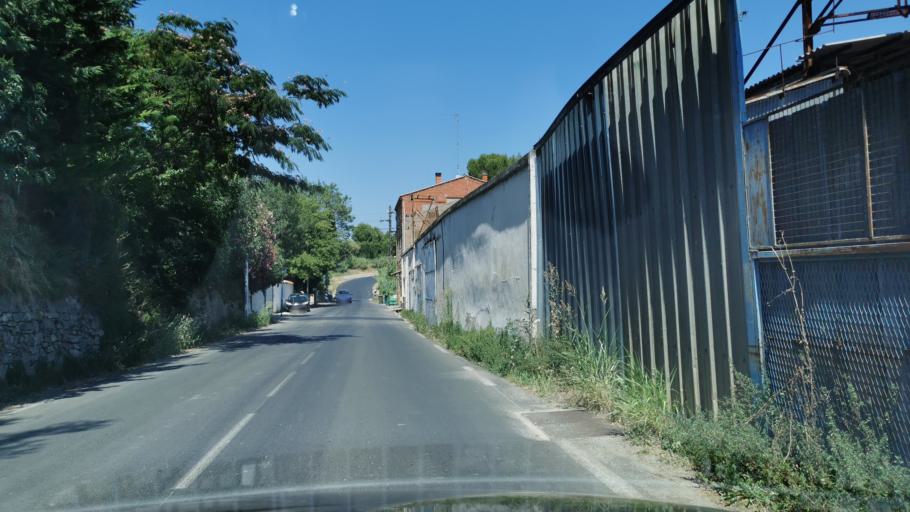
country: FR
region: Languedoc-Roussillon
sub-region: Departement de l'Herault
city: Cazouls-les-Beziers
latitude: 43.3961
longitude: 3.1034
